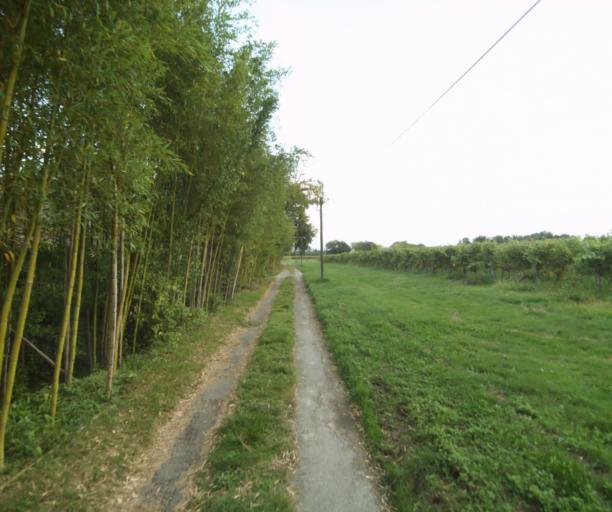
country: FR
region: Aquitaine
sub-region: Departement des Landes
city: Gabarret
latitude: 43.9726
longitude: 0.0901
